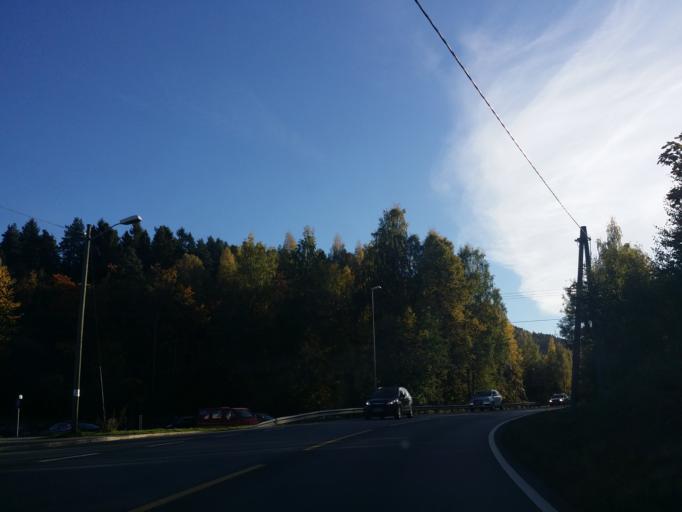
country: NO
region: Buskerud
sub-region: Hole
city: Vik
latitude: 60.0615
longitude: 10.3083
